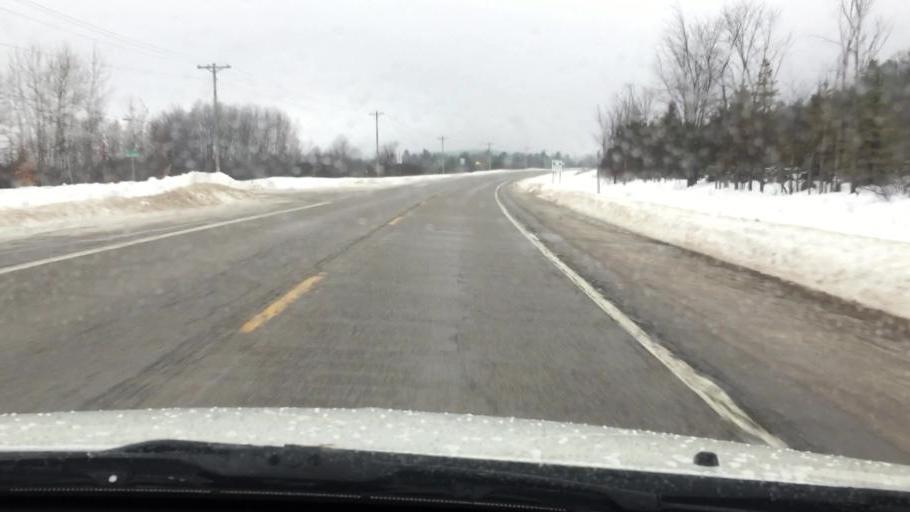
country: US
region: Michigan
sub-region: Charlevoix County
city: East Jordan
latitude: 45.1197
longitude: -85.1299
